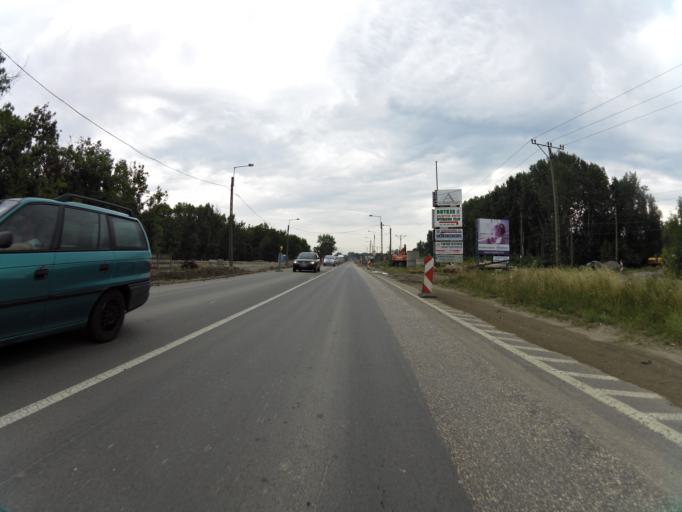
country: HU
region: Csongrad
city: Szeged
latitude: 46.2767
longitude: 20.0982
